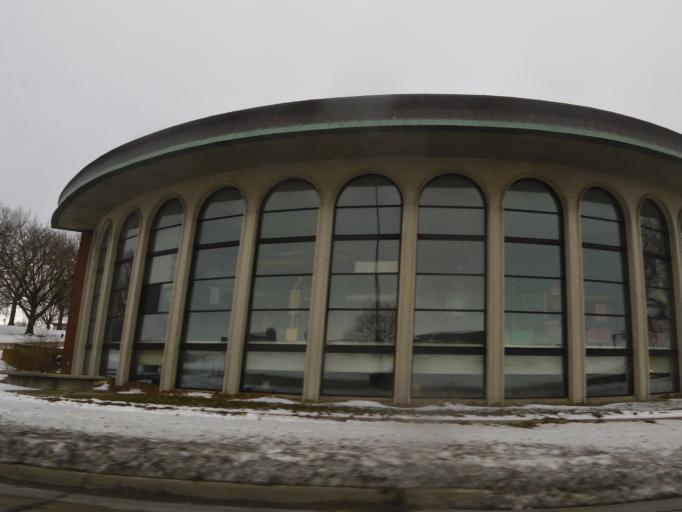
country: US
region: Iowa
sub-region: Black Hawk County
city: Waterloo
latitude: 42.4944
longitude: -92.3451
